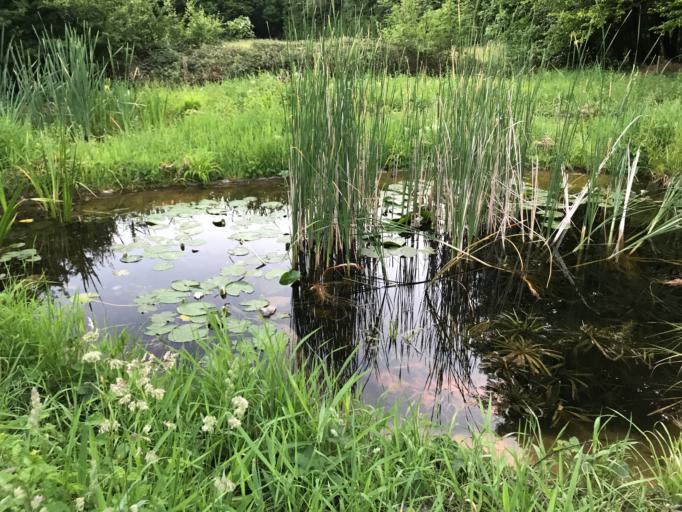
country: CH
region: Basel-City
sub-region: Basel-Stadt
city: Riehen
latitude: 47.5850
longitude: 7.6373
